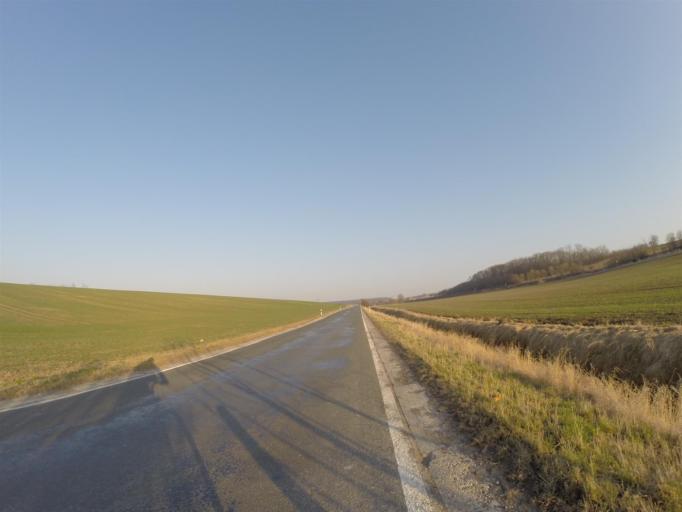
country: DE
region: Thuringia
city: Kleinschwabhausen
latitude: 50.9372
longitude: 11.4489
